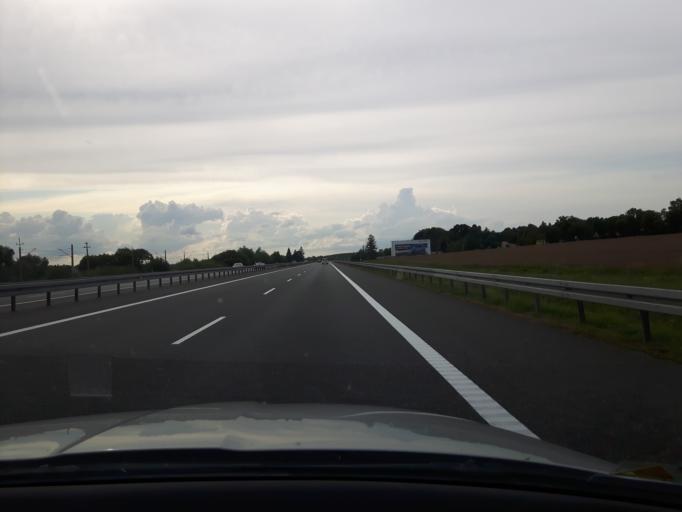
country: PL
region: Warmian-Masurian Voivodeship
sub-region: Powiat elblaski
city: Gronowo Gorne
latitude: 54.1082
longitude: 19.4961
